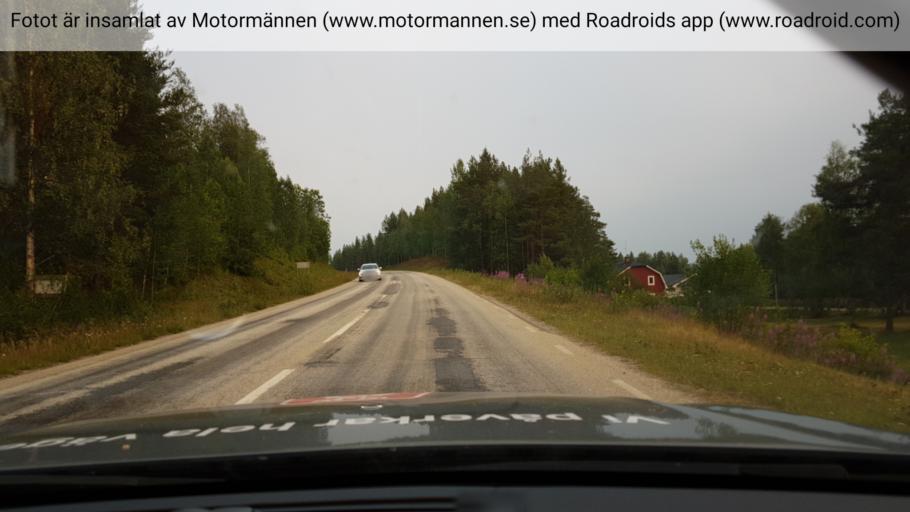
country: SE
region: Jaemtland
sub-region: Harjedalens Kommun
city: Sveg
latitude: 62.4217
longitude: 13.5372
